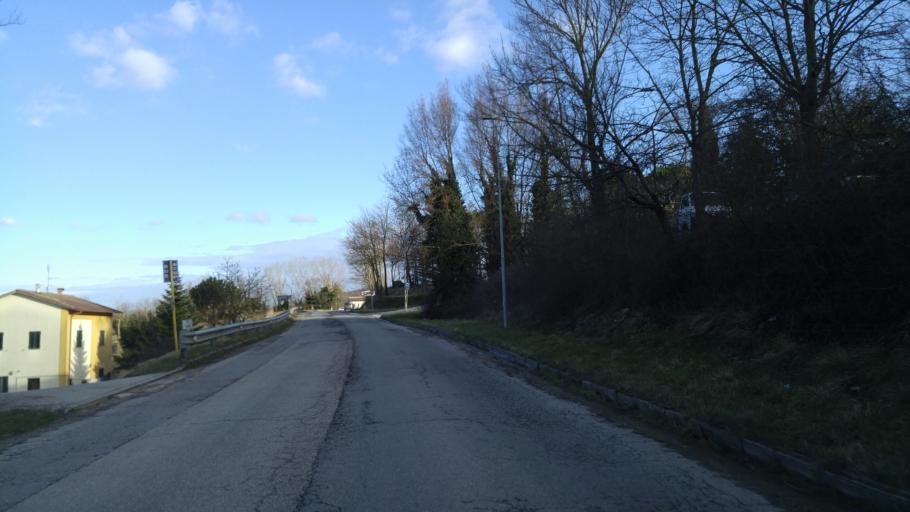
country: IT
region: The Marches
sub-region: Provincia di Pesaro e Urbino
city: Cagli
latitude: 43.5437
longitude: 12.6643
